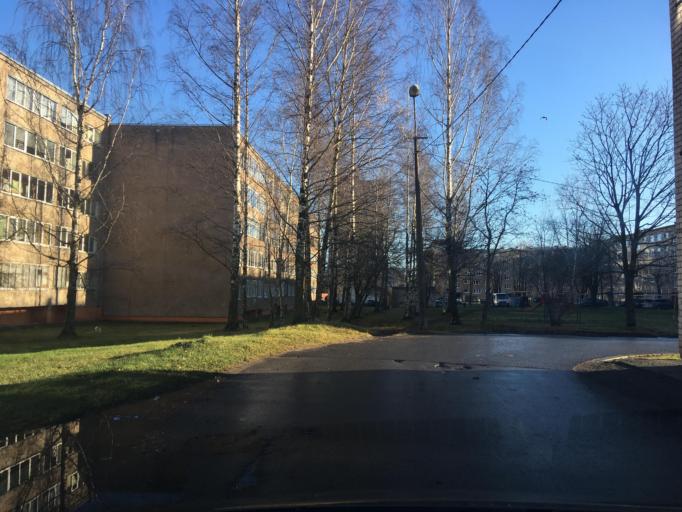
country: EE
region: Ida-Virumaa
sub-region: Narva linn
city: Narva
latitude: 59.3836
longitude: 28.1745
